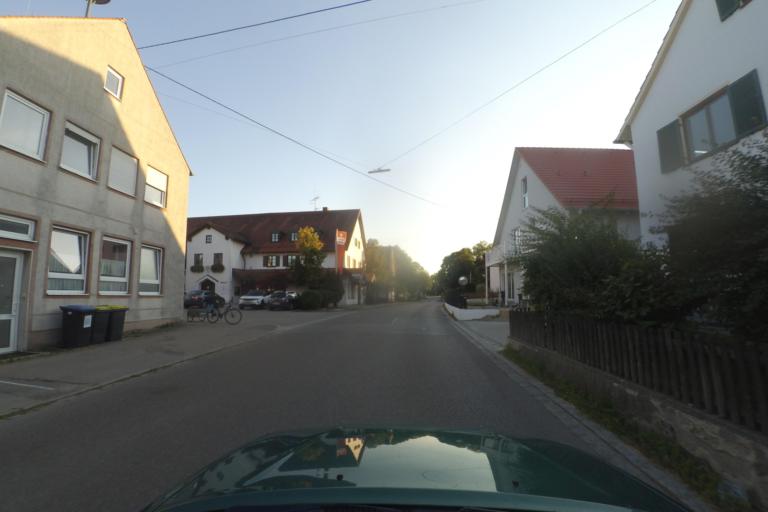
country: DE
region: Bavaria
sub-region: Upper Bavaria
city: Weil
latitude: 48.1160
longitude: 10.9199
